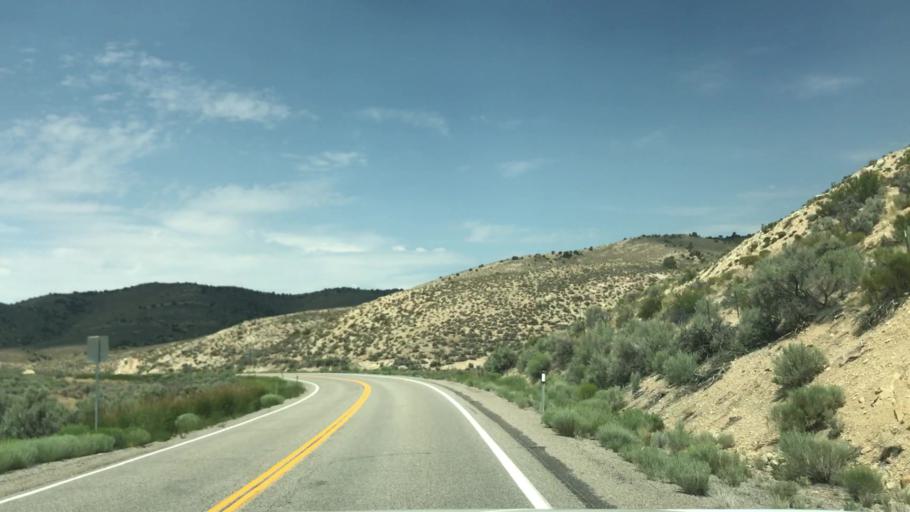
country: US
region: Nevada
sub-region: White Pine County
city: Ely
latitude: 39.3518
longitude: -115.3662
